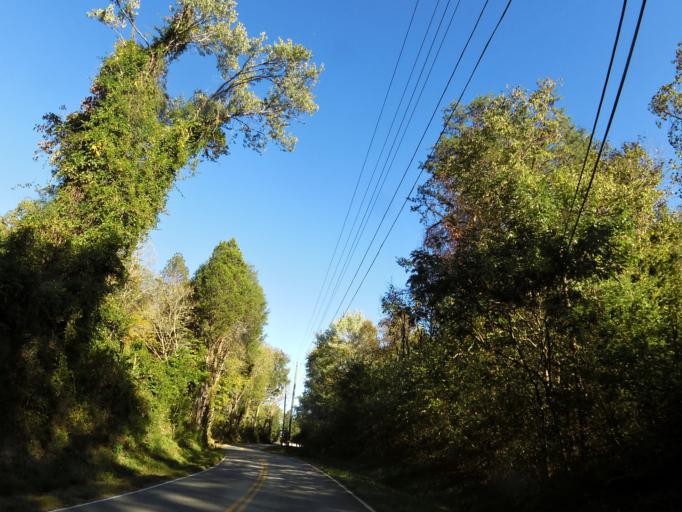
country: US
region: Tennessee
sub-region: Grainger County
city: Rutledge
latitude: 36.2394
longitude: -83.6189
